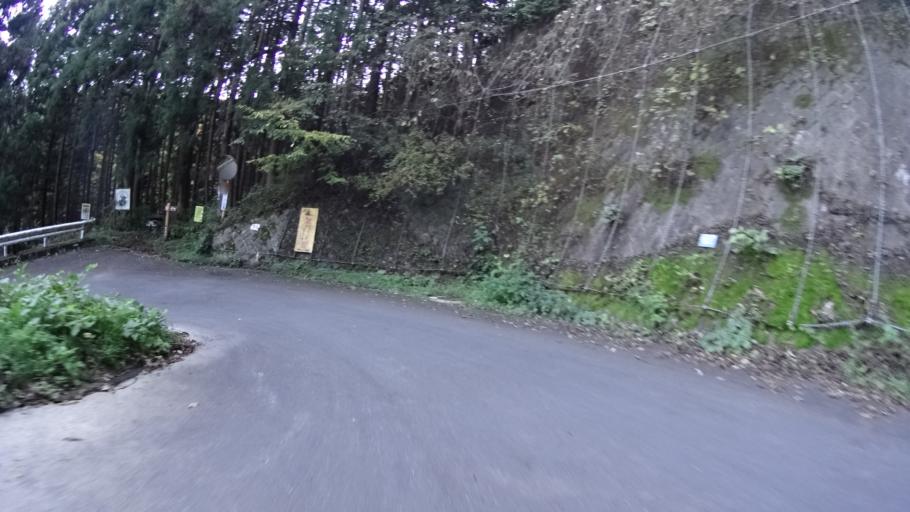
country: JP
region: Yamanashi
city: Uenohara
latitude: 35.6571
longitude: 139.1702
